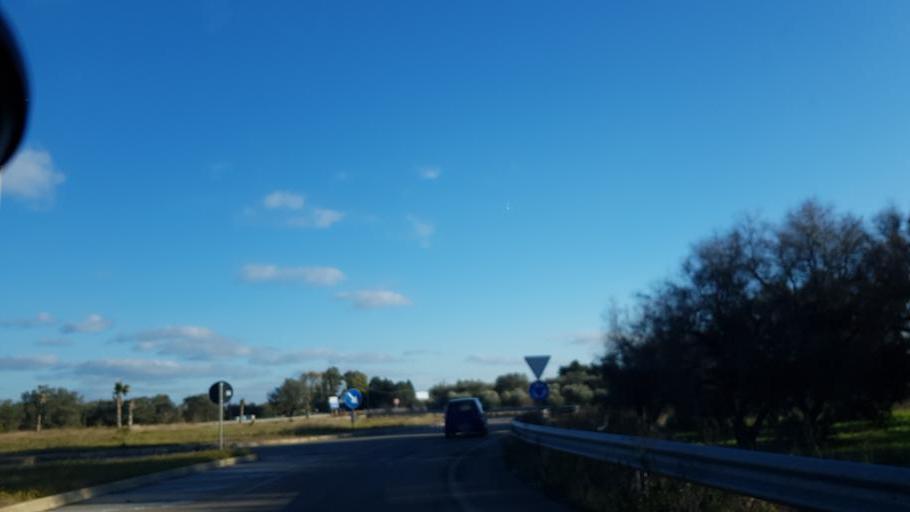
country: IT
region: Apulia
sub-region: Provincia di Brindisi
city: San Pietro Vernotico
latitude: 40.4767
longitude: 18.0072
